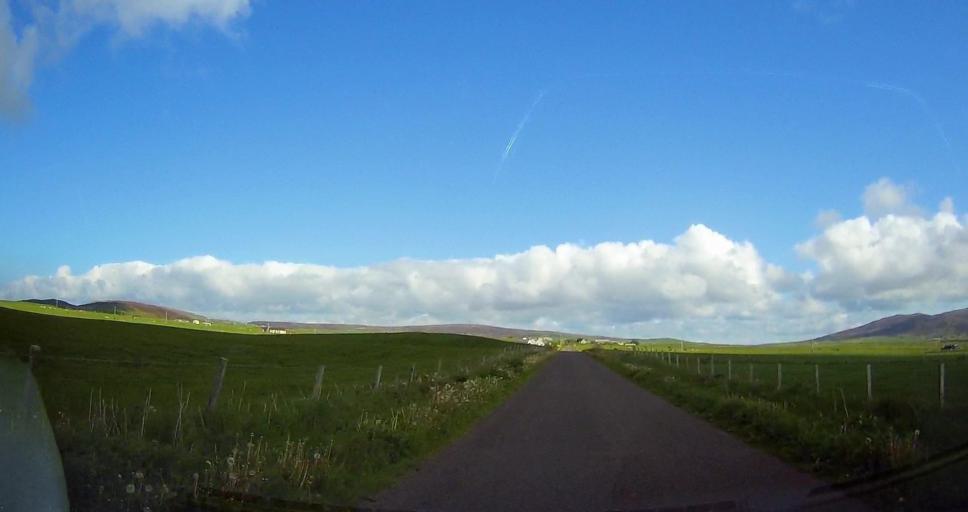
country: GB
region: Scotland
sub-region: Orkney Islands
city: Stromness
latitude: 58.9992
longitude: -3.1704
